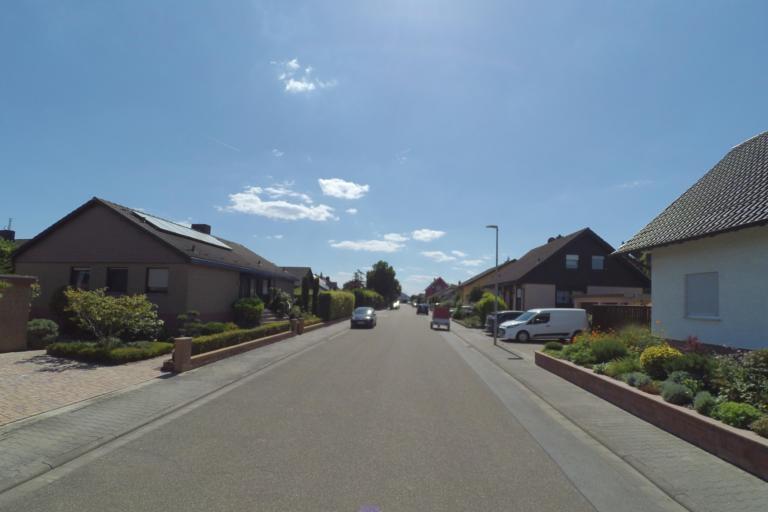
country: DE
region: Hesse
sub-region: Regierungsbezirk Darmstadt
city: Biblis
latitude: 49.6831
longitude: 8.4065
